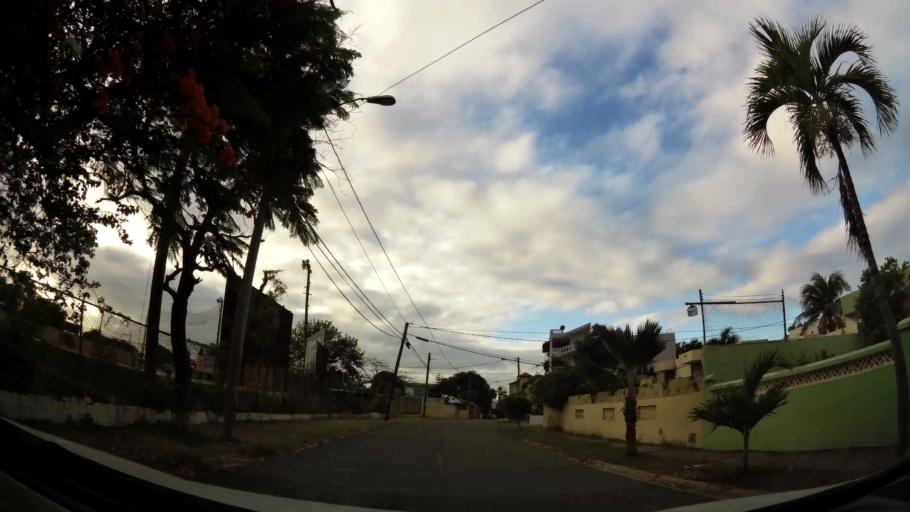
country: DO
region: Nacional
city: Bella Vista
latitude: 18.4326
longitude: -69.9600
